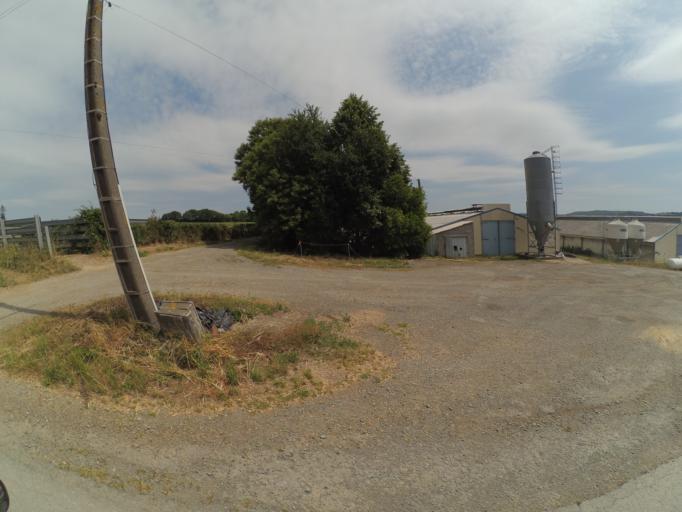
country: FR
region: Pays de la Loire
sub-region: Departement de la Vendee
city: Saint-Paul-en-Pareds
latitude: 46.8580
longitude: -0.9637
